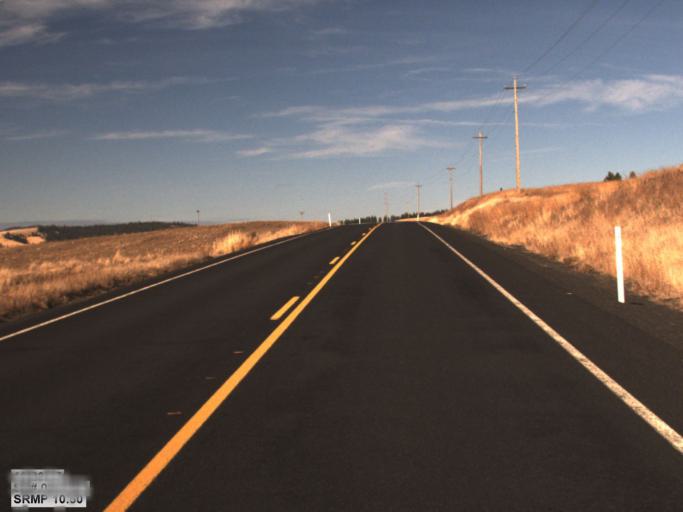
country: US
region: Washington
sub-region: Lincoln County
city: Davenport
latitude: 47.8005
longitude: -118.1737
